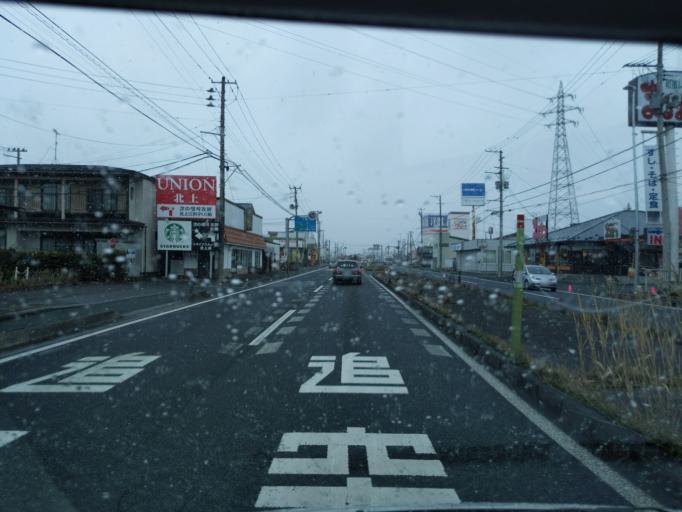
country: JP
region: Iwate
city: Kitakami
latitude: 39.2914
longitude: 141.1049
